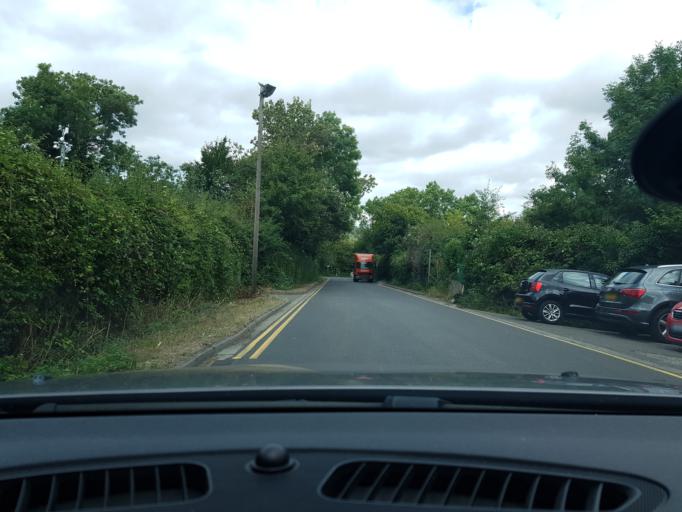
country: GB
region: England
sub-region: Buckinghamshire
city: Iver
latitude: 51.4885
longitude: -0.4860
